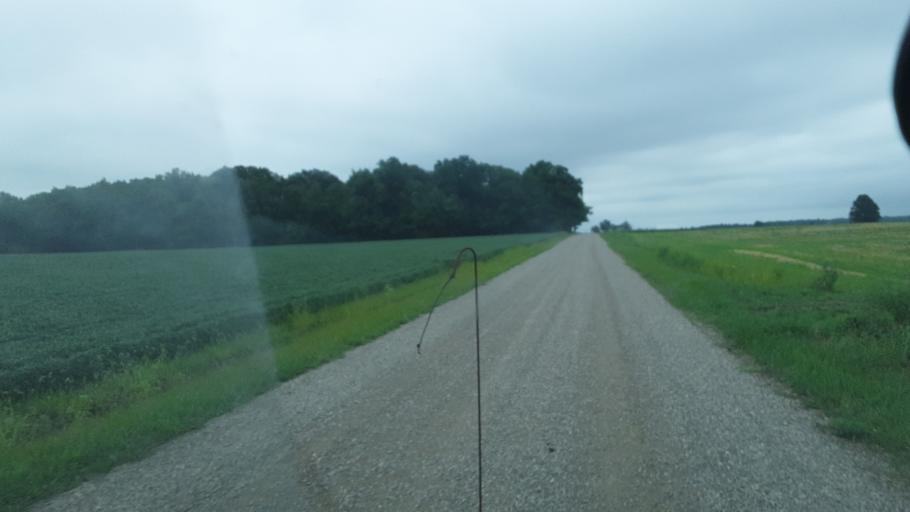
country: US
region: Indiana
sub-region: Adams County
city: Geneva
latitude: 40.6201
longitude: -85.0080
